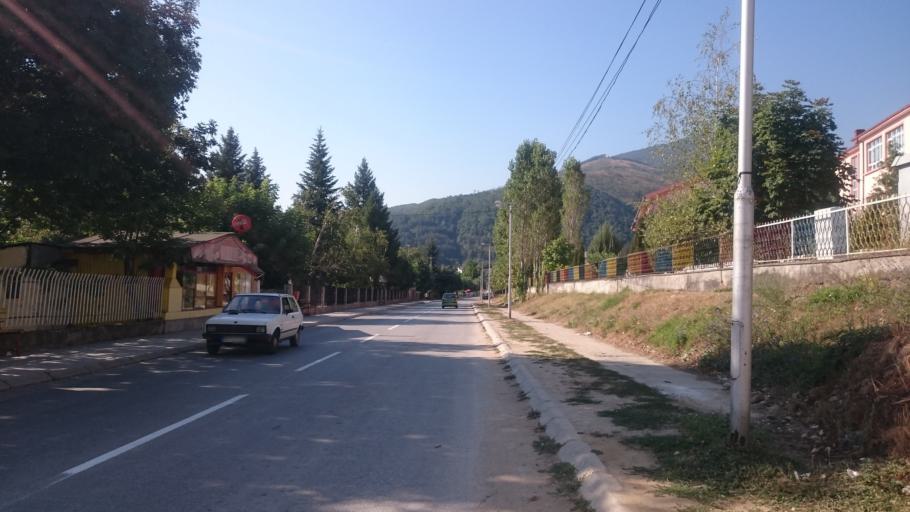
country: MK
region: Makedonski Brod
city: Makedonski Brod
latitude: 41.5123
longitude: 21.2165
